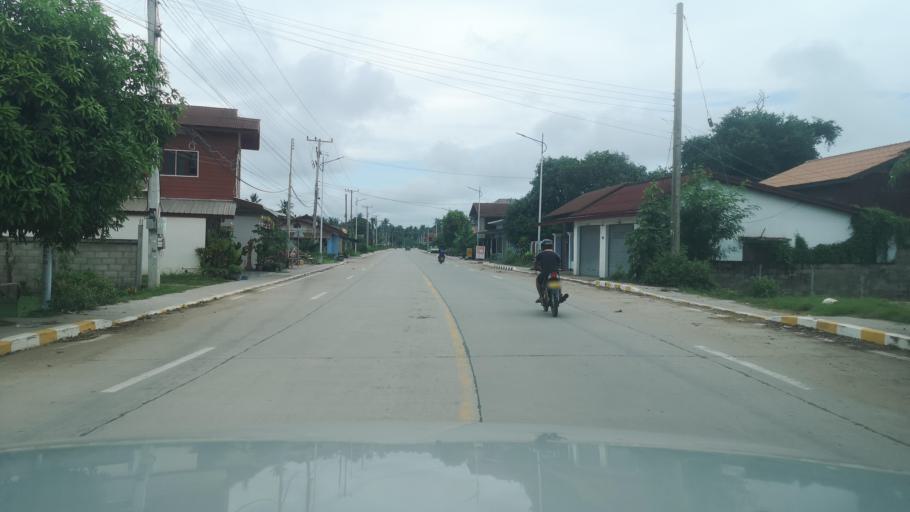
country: TH
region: Nong Khai
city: Tha Bo
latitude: 17.8268
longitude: 102.6537
